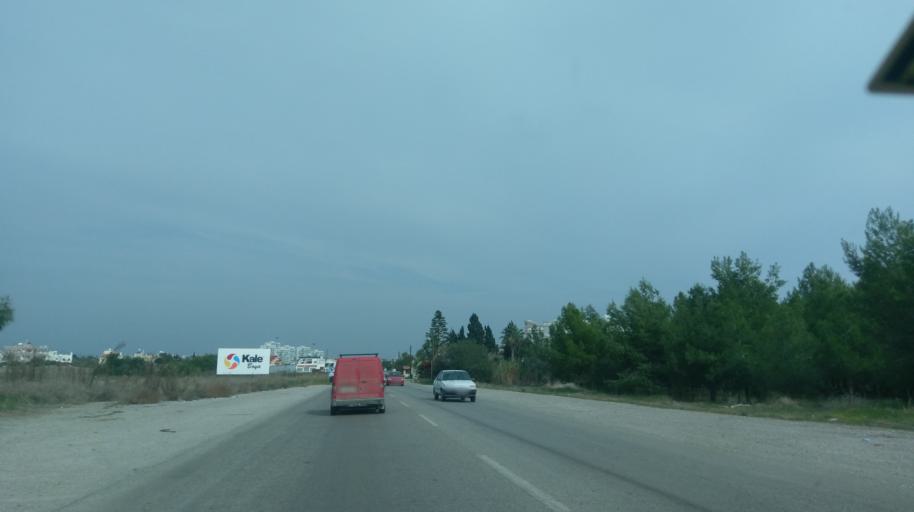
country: CY
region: Ammochostos
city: Trikomo
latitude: 35.2965
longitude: 33.9351
